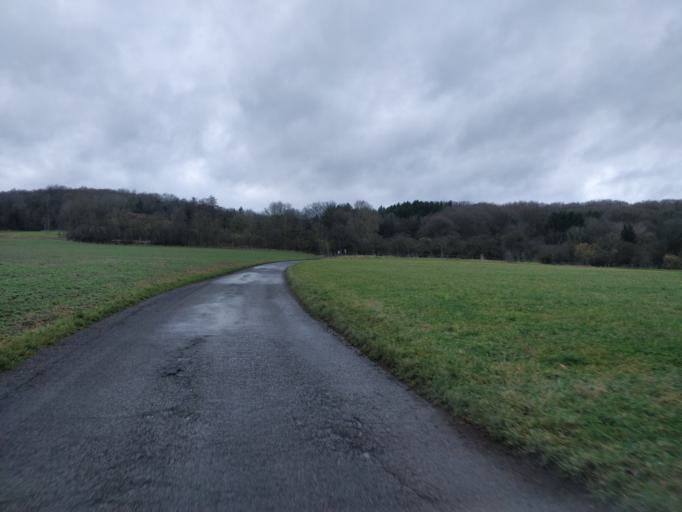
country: DE
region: Rheinland-Pfalz
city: Leutesdorf
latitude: 50.4587
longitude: 7.4051
